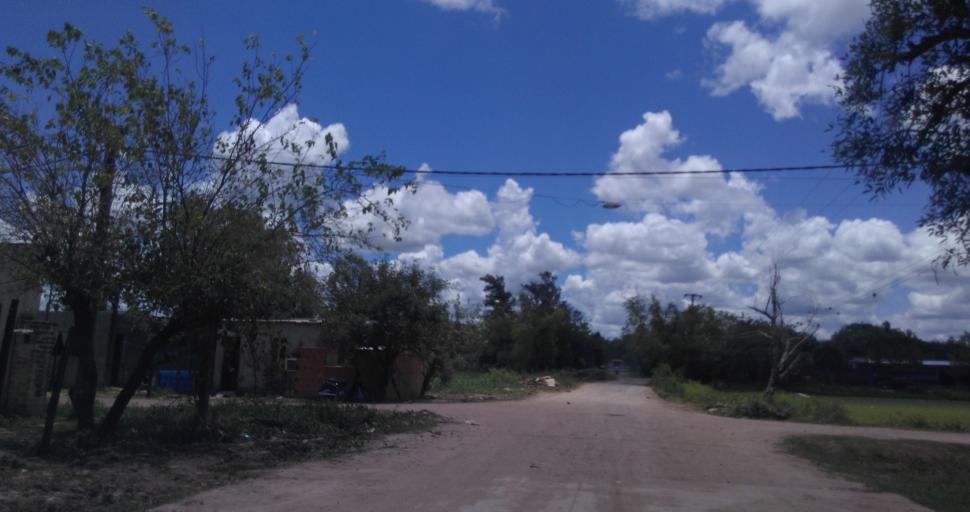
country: AR
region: Chaco
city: Resistencia
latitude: -27.4380
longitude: -58.9743
